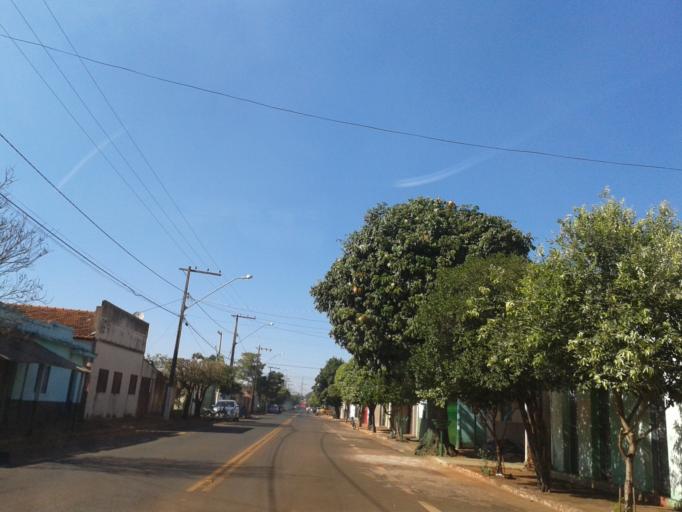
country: BR
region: Minas Gerais
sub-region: Capinopolis
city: Capinopolis
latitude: -18.5128
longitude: -49.5030
